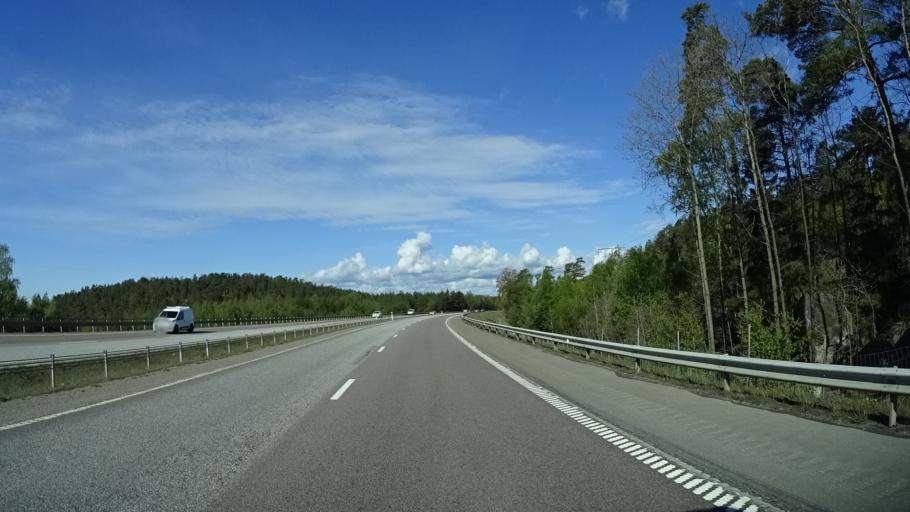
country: SE
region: OEstergoetland
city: Lindo
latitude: 58.6712
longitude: 16.2420
